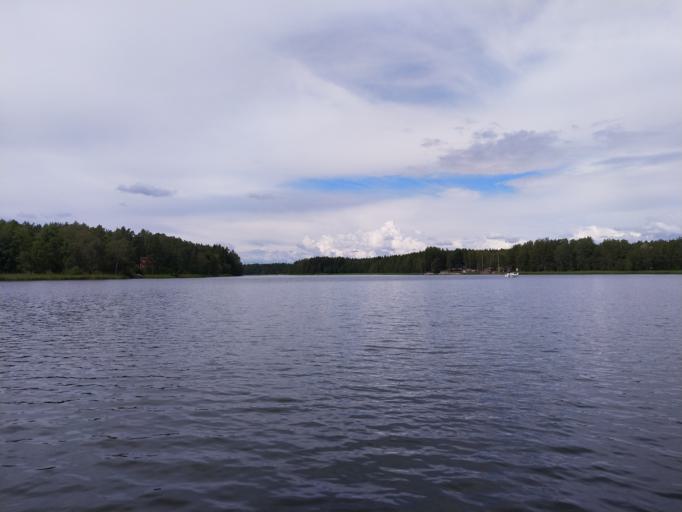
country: FI
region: Uusimaa
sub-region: Raaseporin
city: Karis
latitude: 59.9687
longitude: 23.7038
